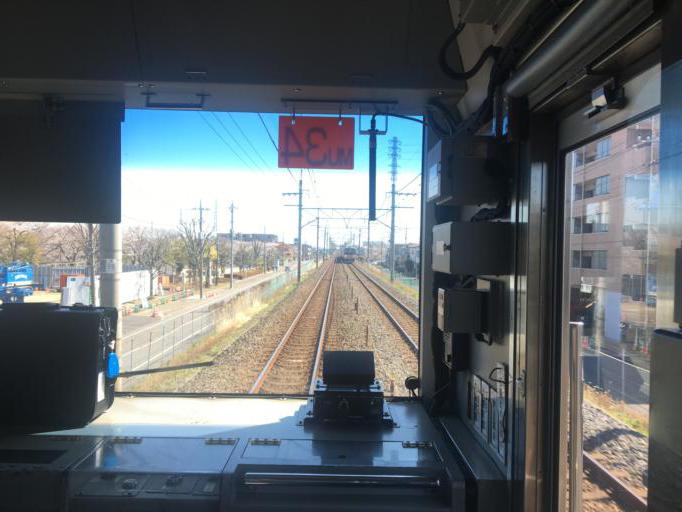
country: JP
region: Saitama
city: Koshigaya
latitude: 35.8750
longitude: 139.7522
